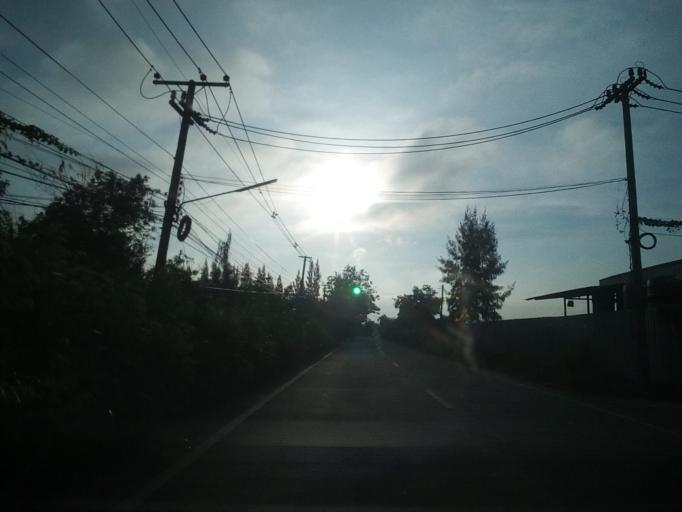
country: TH
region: Lamphun
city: Ban Thi
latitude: 18.6296
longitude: 99.0652
